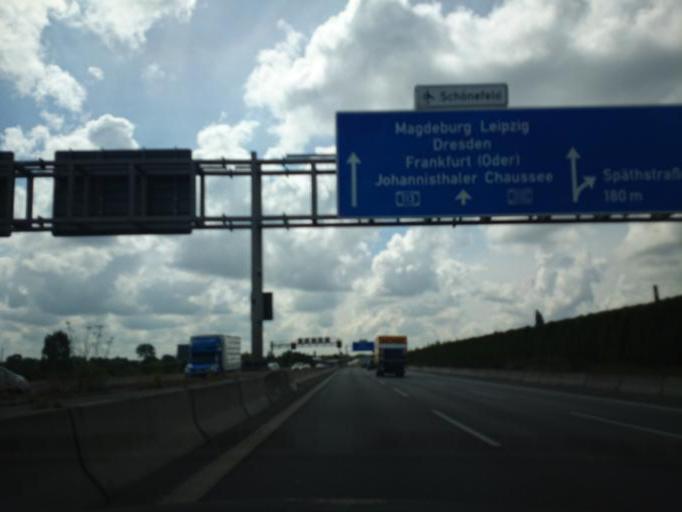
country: DE
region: Berlin
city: Plaenterwald
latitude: 52.4587
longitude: 13.4581
